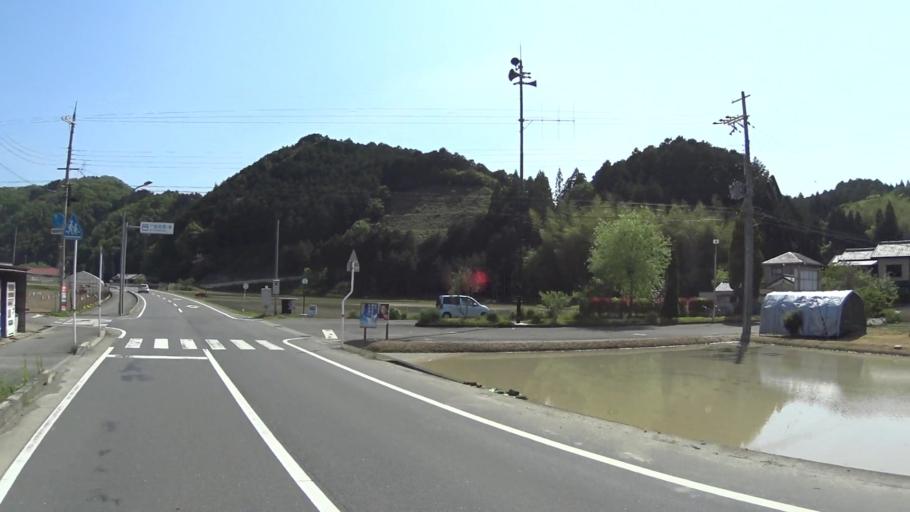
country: JP
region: Kyoto
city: Kameoka
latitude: 35.1330
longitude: 135.4931
